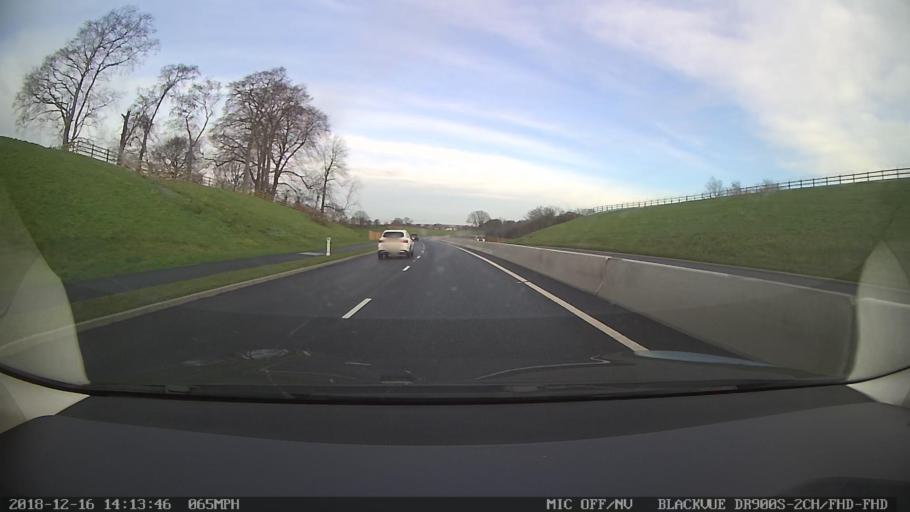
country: GB
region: England
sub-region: Cheshire East
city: Poynton
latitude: 53.3609
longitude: -2.1256
